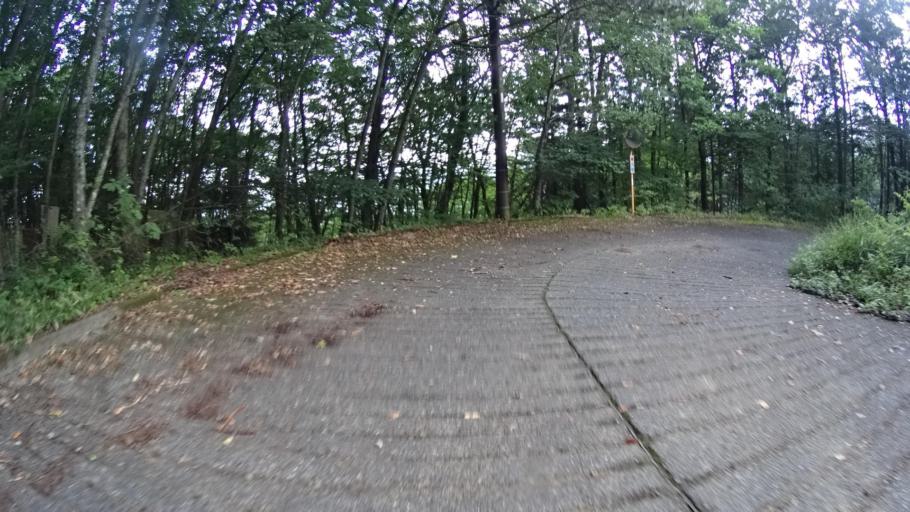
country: JP
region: Yamanashi
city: Uenohara
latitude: 35.7467
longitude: 139.0563
